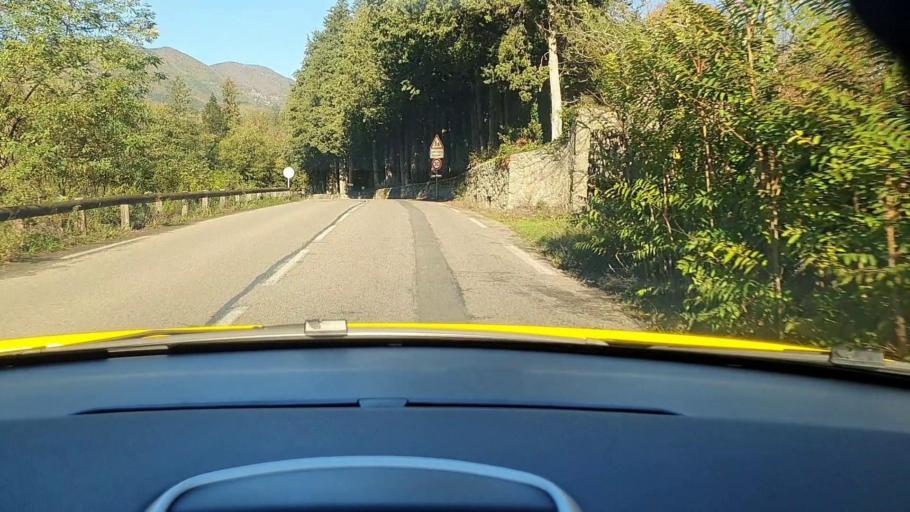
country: FR
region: Languedoc-Roussillon
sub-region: Departement du Gard
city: Le Vigan
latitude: 43.9880
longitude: 3.5823
